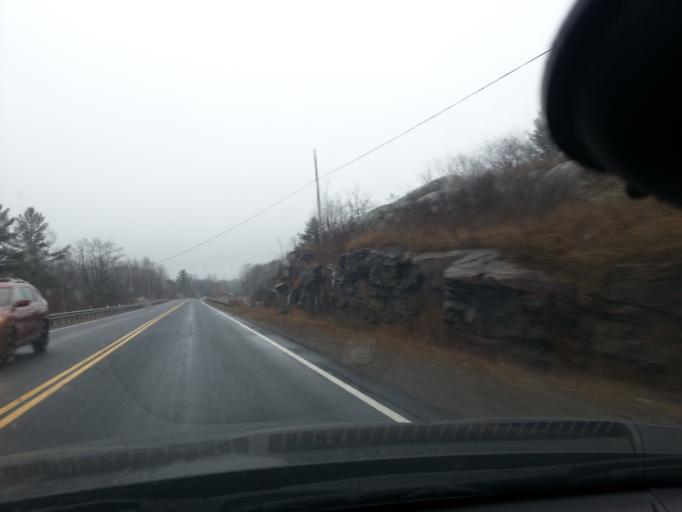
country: CA
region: Ontario
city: Greater Napanee
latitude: 44.6136
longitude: -77.1790
